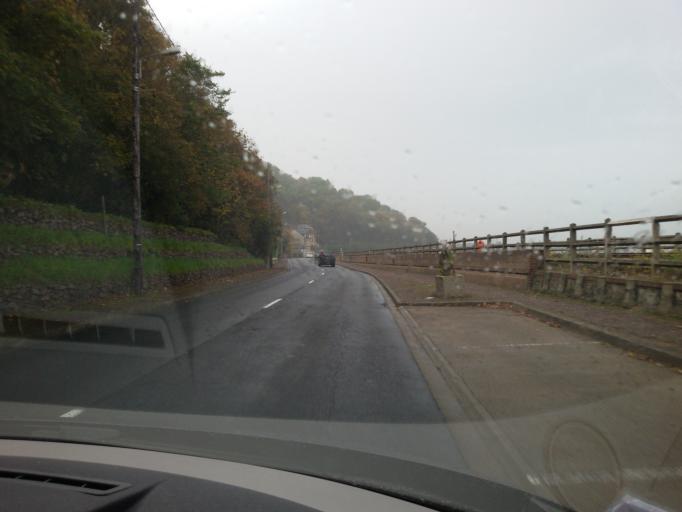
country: FR
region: Lower Normandy
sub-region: Departement du Calvados
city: Houlgate
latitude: 49.2974
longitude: -0.0864
